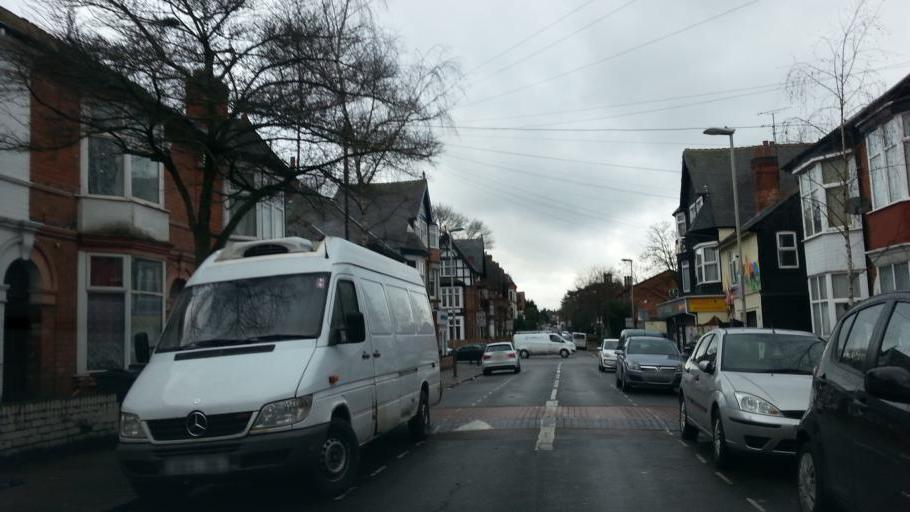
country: GB
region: England
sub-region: City of Leicester
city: Leicester
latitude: 52.6248
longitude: -1.1515
